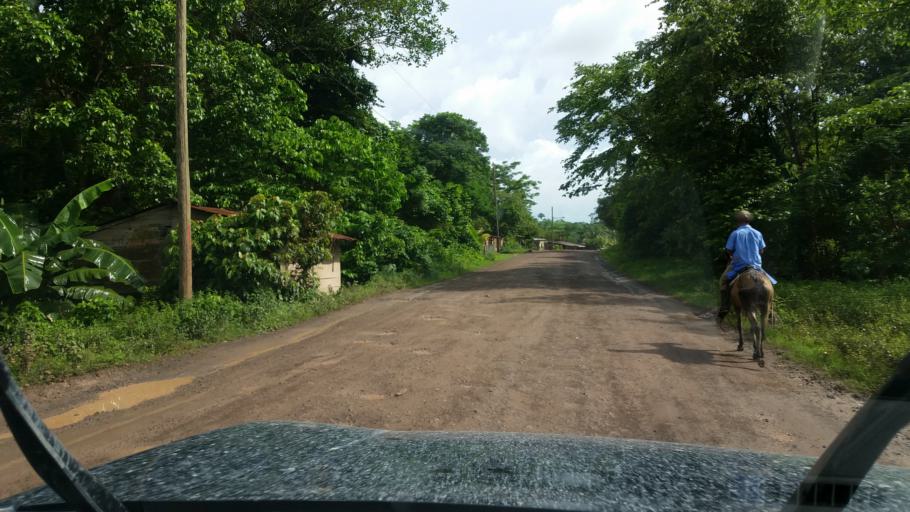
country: NI
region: Atlantico Norte (RAAN)
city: Siuna
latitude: 13.6031
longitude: -84.7987
